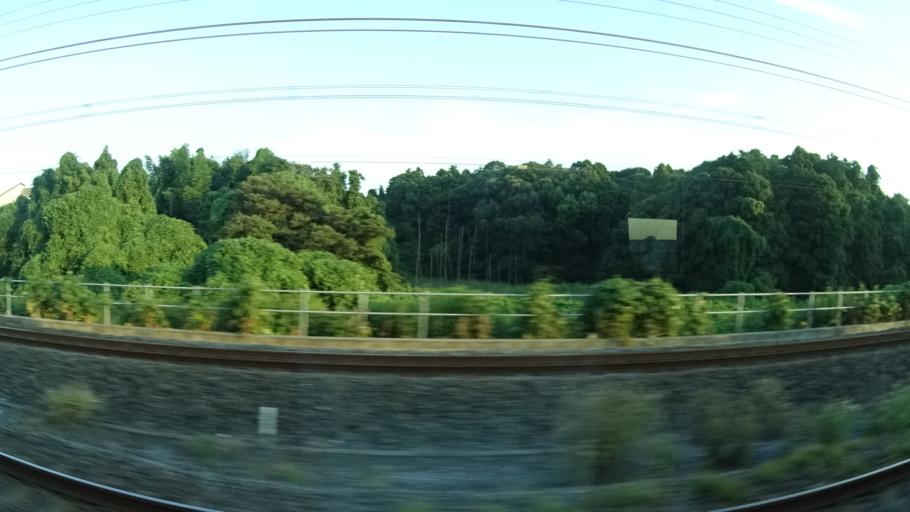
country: JP
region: Chiba
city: Abiko
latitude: 35.8733
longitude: 140.0219
